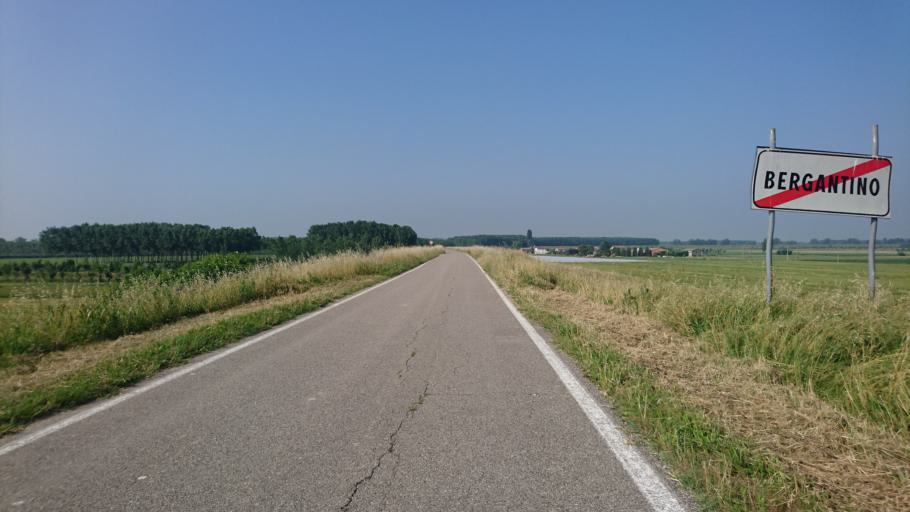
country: IT
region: Veneto
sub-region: Provincia di Rovigo
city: Bergantino
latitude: 45.0548
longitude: 11.2478
